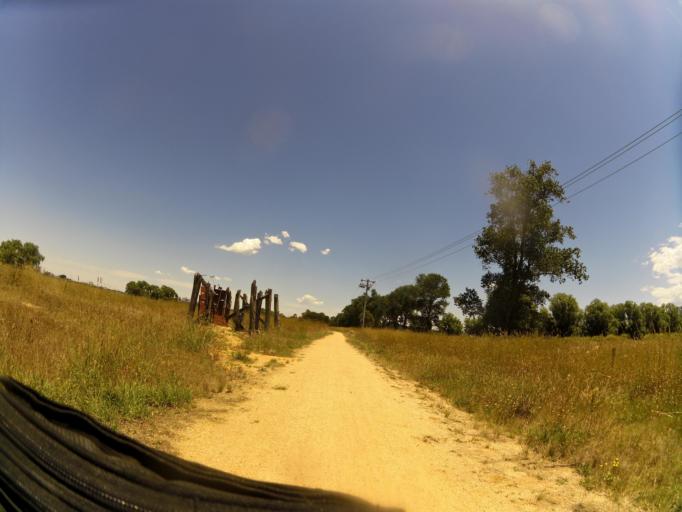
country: AU
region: Victoria
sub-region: Wellington
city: Heyfield
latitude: -37.9703
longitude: 146.9550
